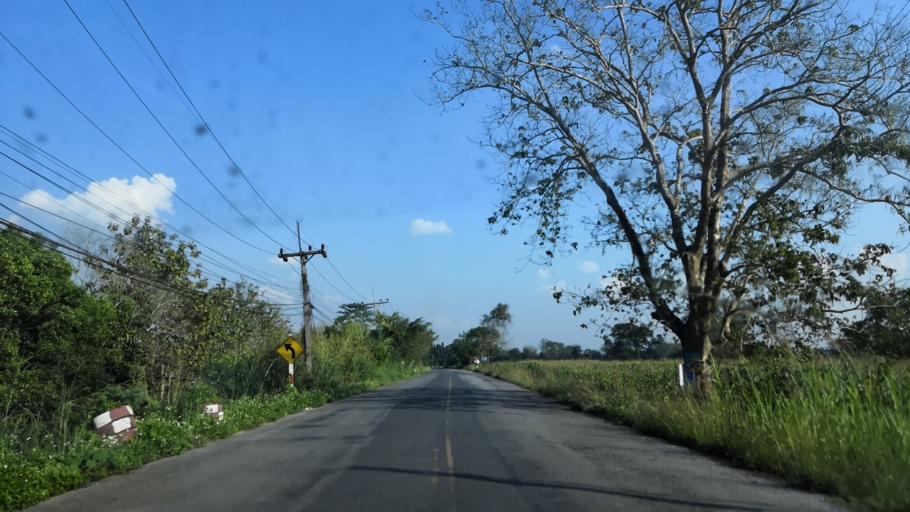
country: TH
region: Chiang Rai
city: Wiang Chai
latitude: 19.9482
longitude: 99.9221
